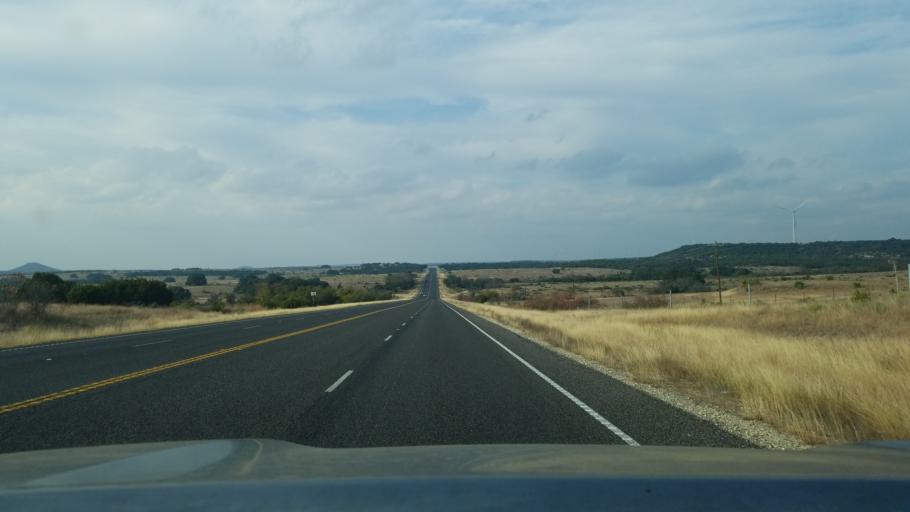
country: US
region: Texas
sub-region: Mills County
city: Goldthwaite
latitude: 31.3212
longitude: -98.4892
